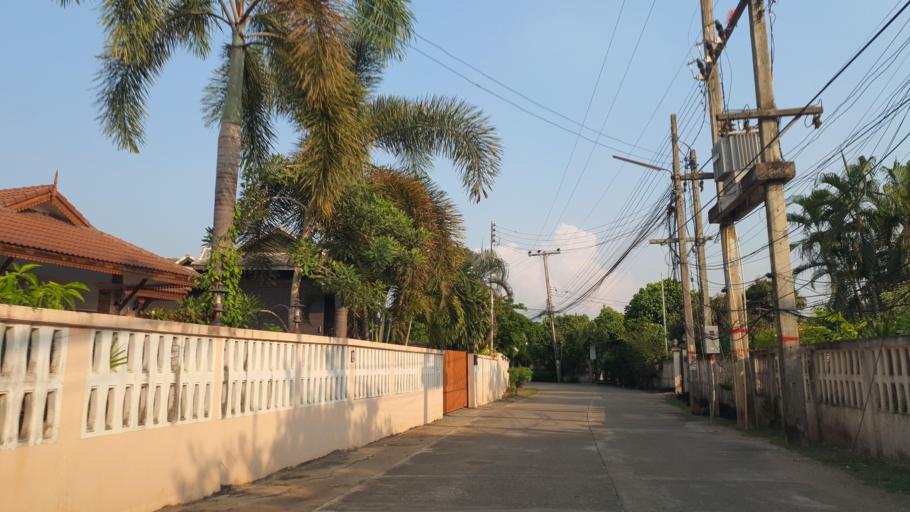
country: TH
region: Chiang Mai
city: San Pa Tong
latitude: 18.6390
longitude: 98.8602
